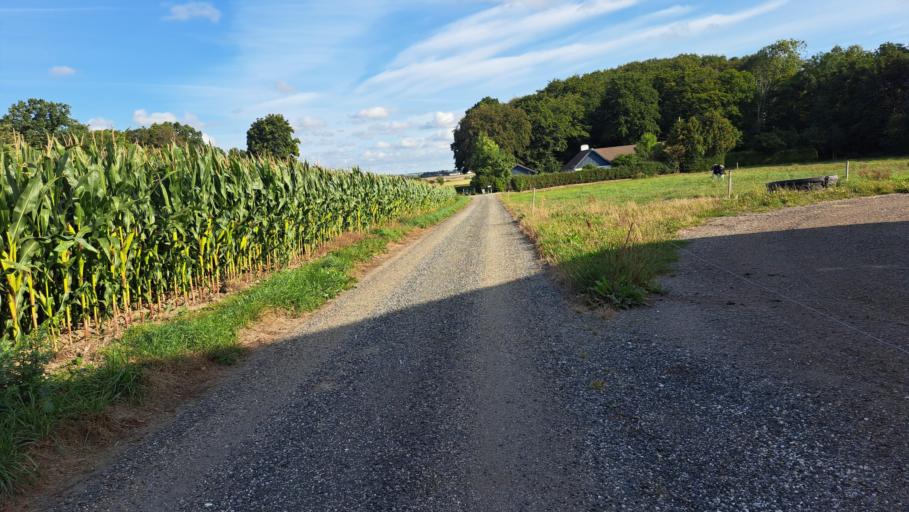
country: DK
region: Central Jutland
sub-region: Hedensted Kommune
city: Hedensted
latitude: 55.8193
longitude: 9.6973
